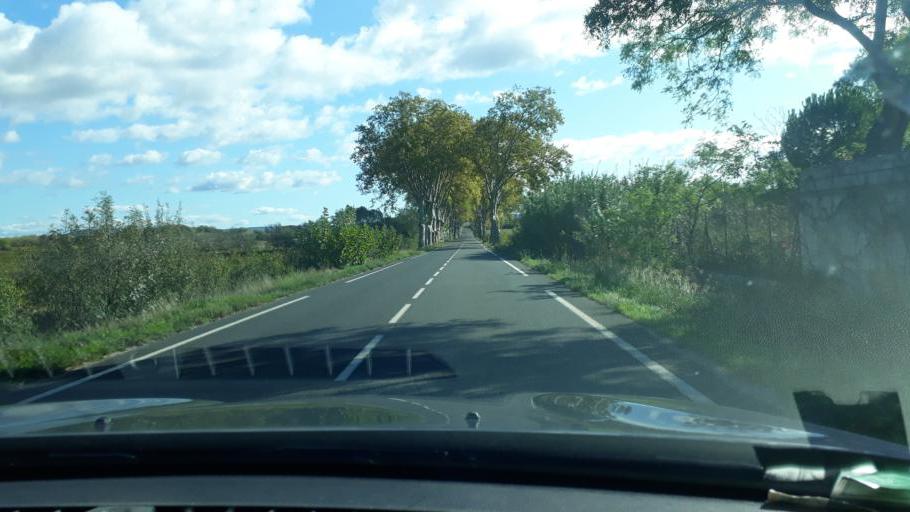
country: FR
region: Languedoc-Roussillon
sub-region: Departement de l'Herault
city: Saint-Andre-de-Sangonis
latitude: 43.6543
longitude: 3.4861
